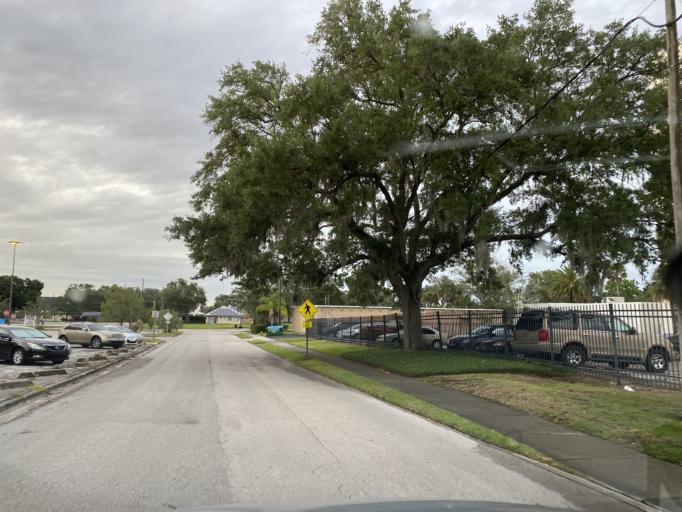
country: US
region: Florida
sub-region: Seminole County
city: Sanford
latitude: 28.8108
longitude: -81.2639
